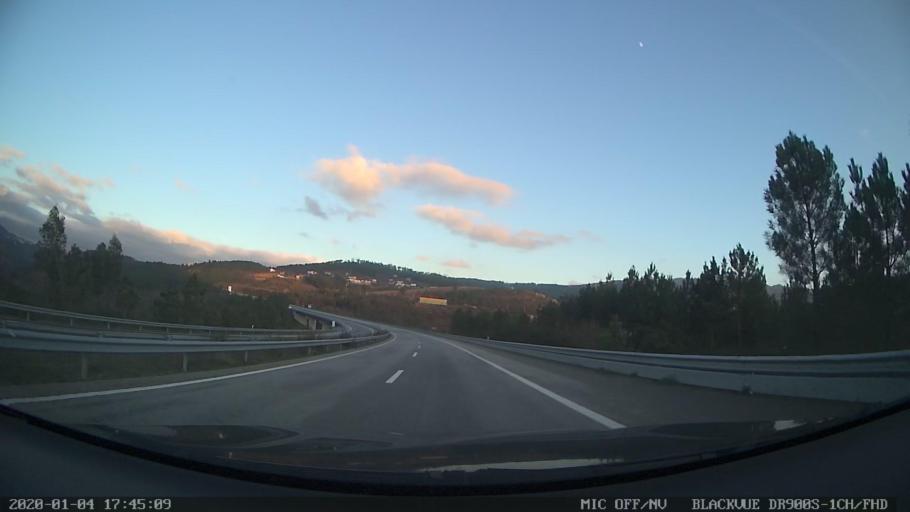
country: PT
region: Vila Real
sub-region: Mondim de Basto
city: Mondim de Basto
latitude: 41.4706
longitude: -7.9414
